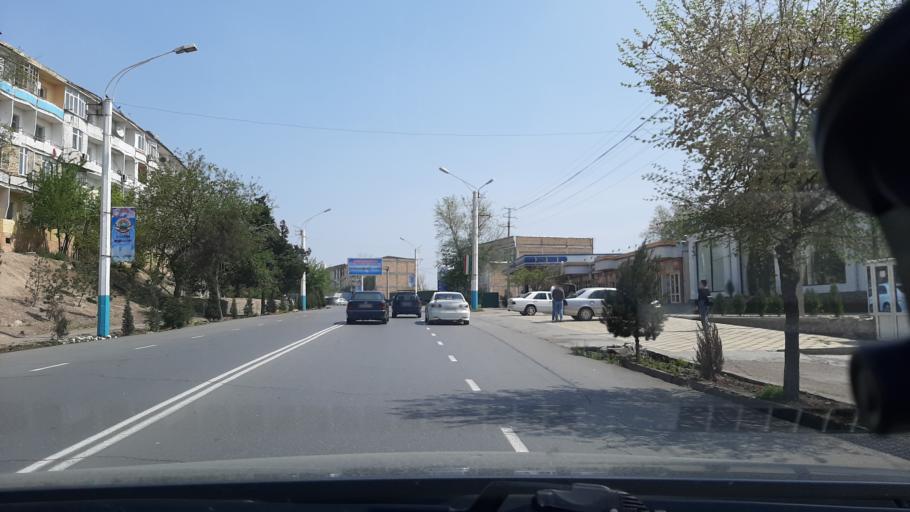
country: TJ
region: Viloyati Sughd
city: Khujand
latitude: 40.2949
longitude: 69.6054
